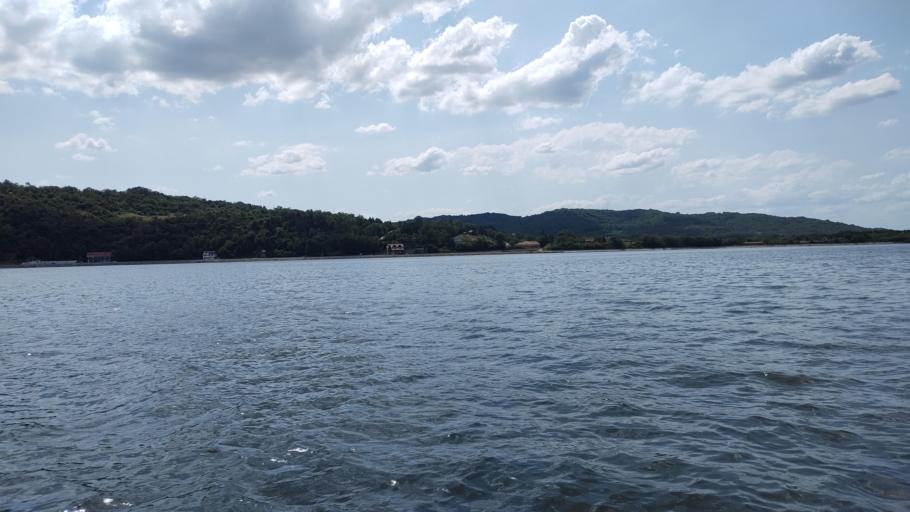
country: RS
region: Central Serbia
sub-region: Branicevski Okrug
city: Golubac
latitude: 44.6659
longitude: 21.6225
